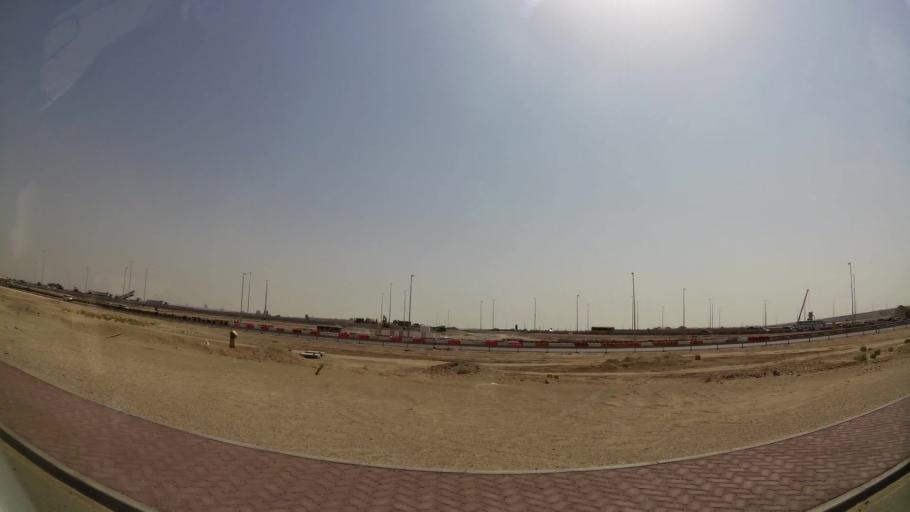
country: AE
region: Abu Dhabi
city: Abu Dhabi
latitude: 24.2925
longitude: 54.5604
